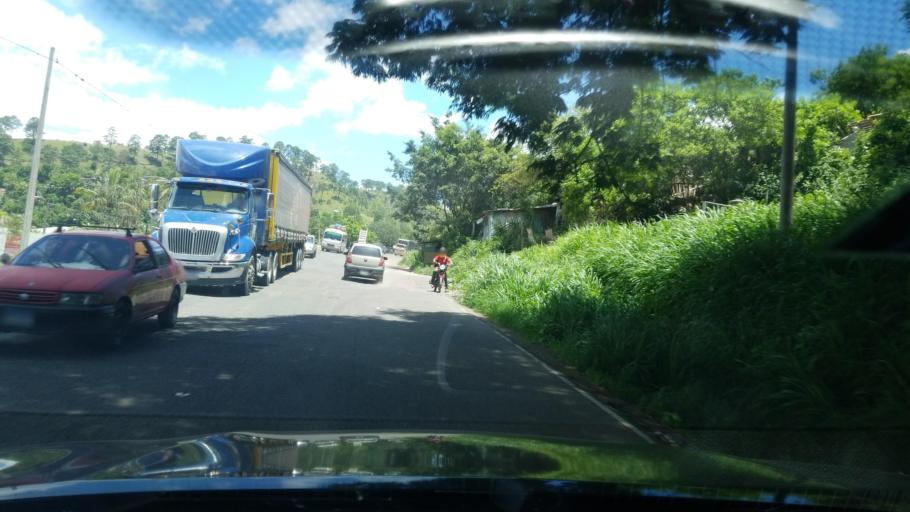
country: HN
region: Francisco Morazan
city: Rio Abajo
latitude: 14.1452
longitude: -87.2242
